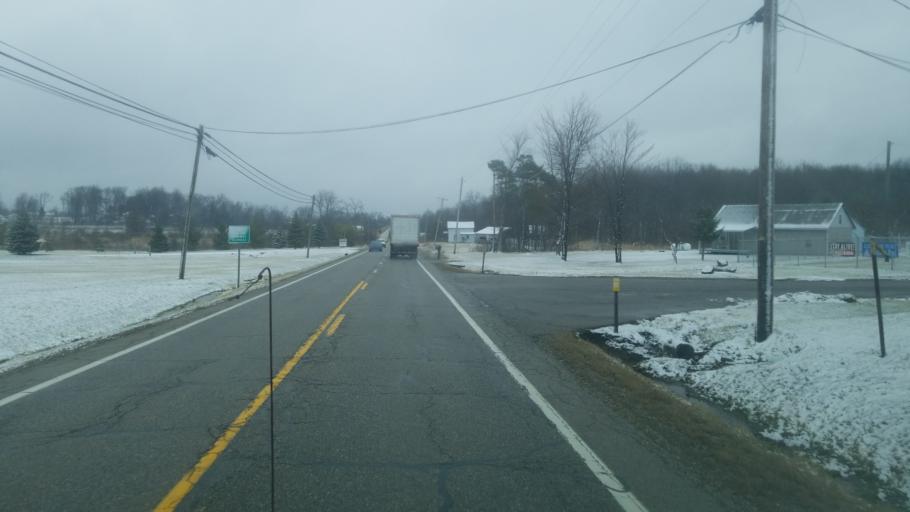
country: US
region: Ohio
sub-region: Portage County
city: Garrettsville
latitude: 41.2381
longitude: -81.1328
